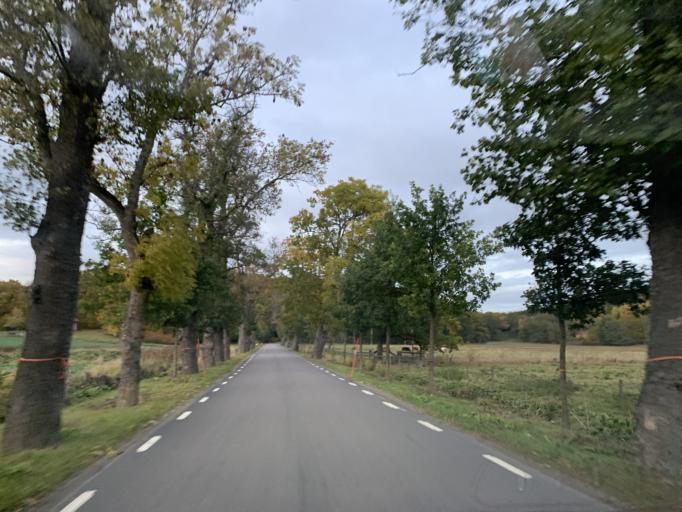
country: SE
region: Stockholm
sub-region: Nynashamns Kommun
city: Osmo
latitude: 58.9598
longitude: 17.7675
